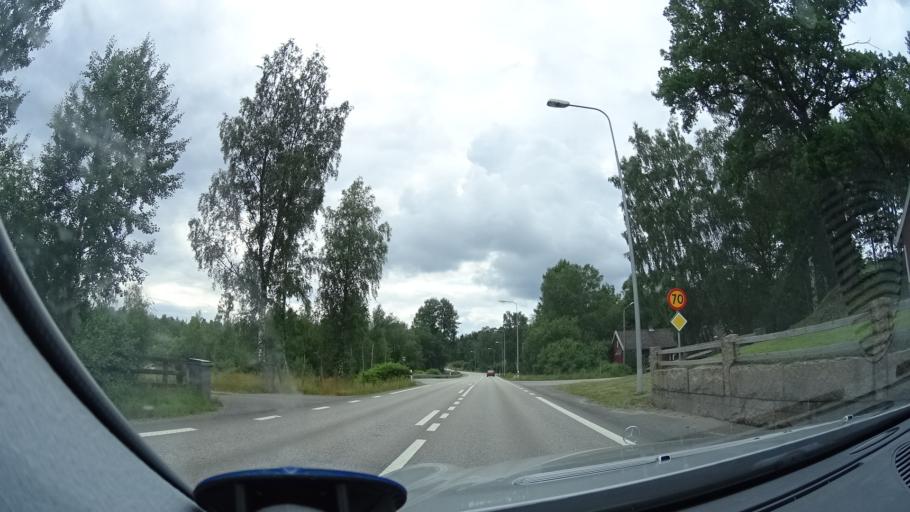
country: SE
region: Kronoberg
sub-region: Tingsryds Kommun
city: Tingsryd
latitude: 56.5005
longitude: 15.0491
